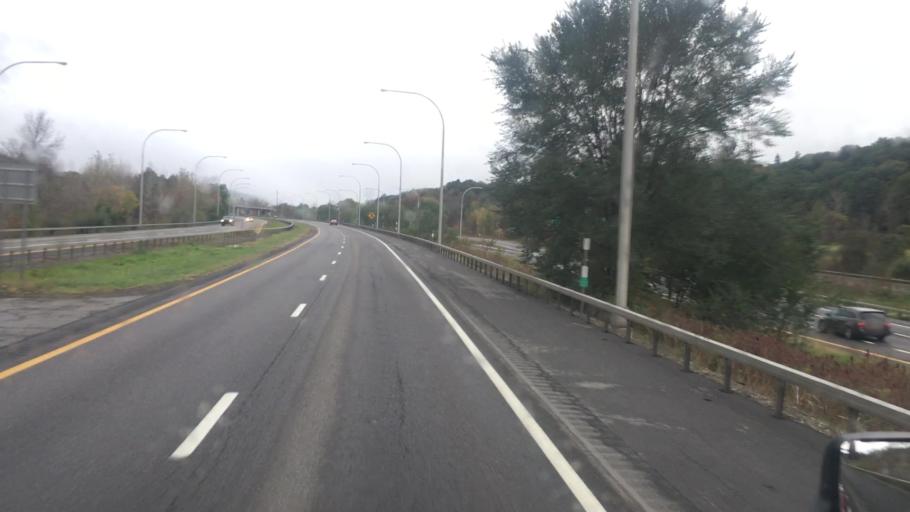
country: US
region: New York
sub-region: Broome County
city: Endwell
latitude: 42.1147
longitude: -76.0007
